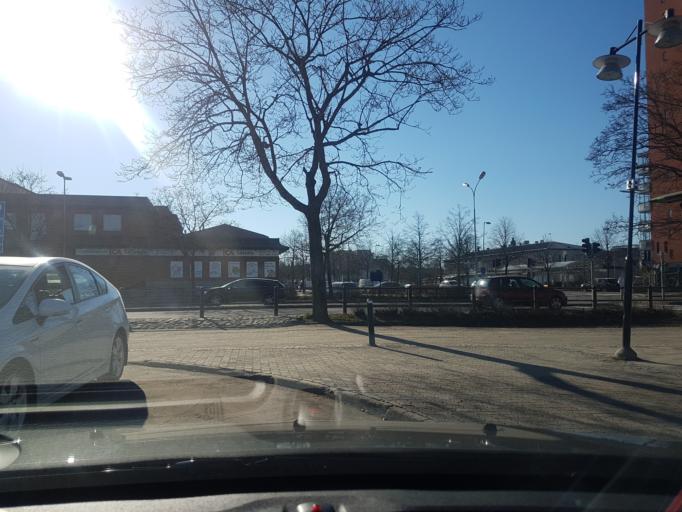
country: SE
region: Stockholm
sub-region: Sigtuna Kommun
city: Marsta
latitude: 59.6278
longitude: 17.8609
